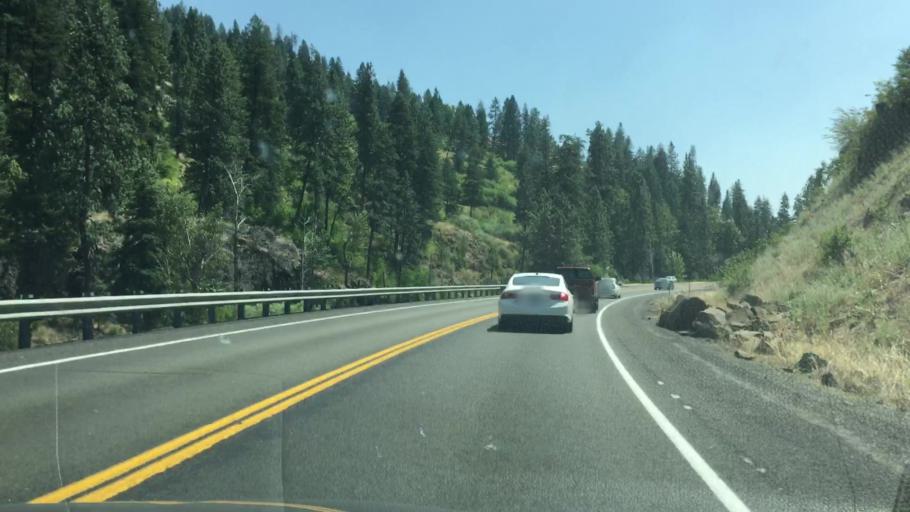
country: US
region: Idaho
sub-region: Valley County
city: McCall
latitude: 45.2358
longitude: -116.3264
